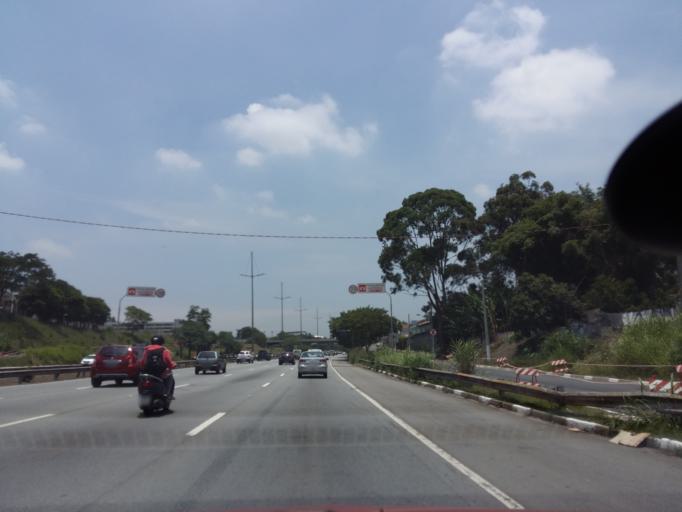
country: BR
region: Sao Paulo
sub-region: Diadema
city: Diadema
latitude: -23.6435
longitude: -46.6310
